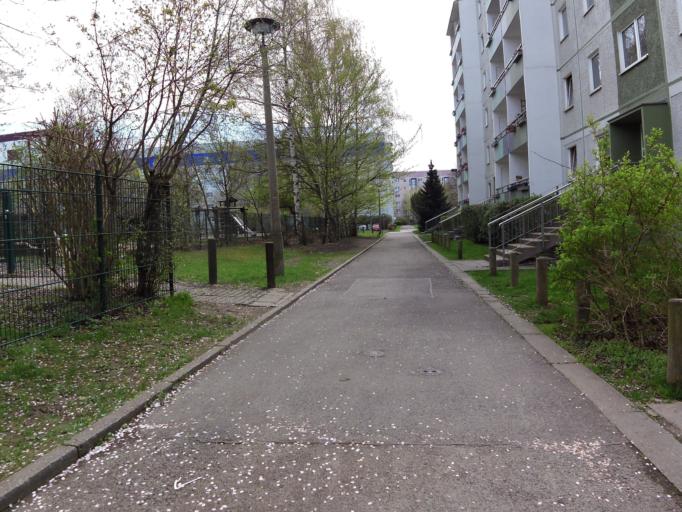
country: DE
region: Saxony
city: Markranstadt
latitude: 51.3120
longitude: 12.2623
